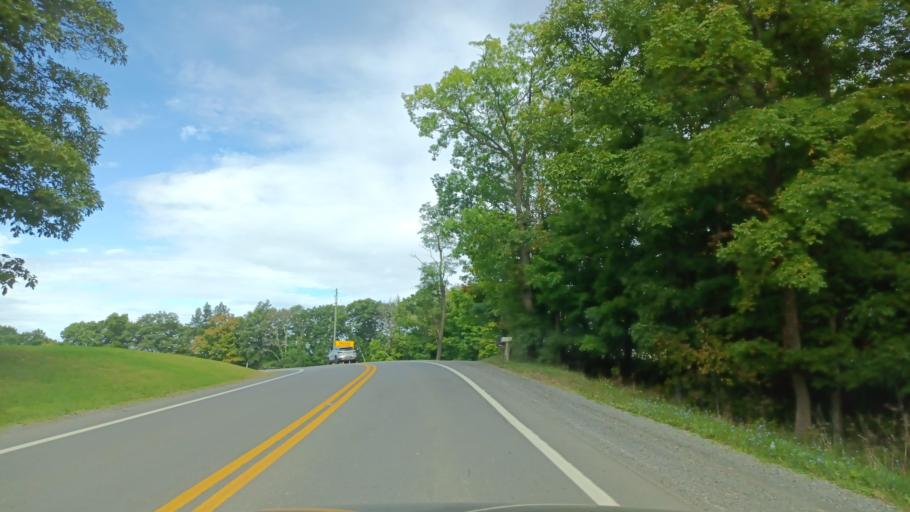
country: US
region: Maryland
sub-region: Garrett County
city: Mountain Lake Park
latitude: 39.2868
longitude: -79.3208
